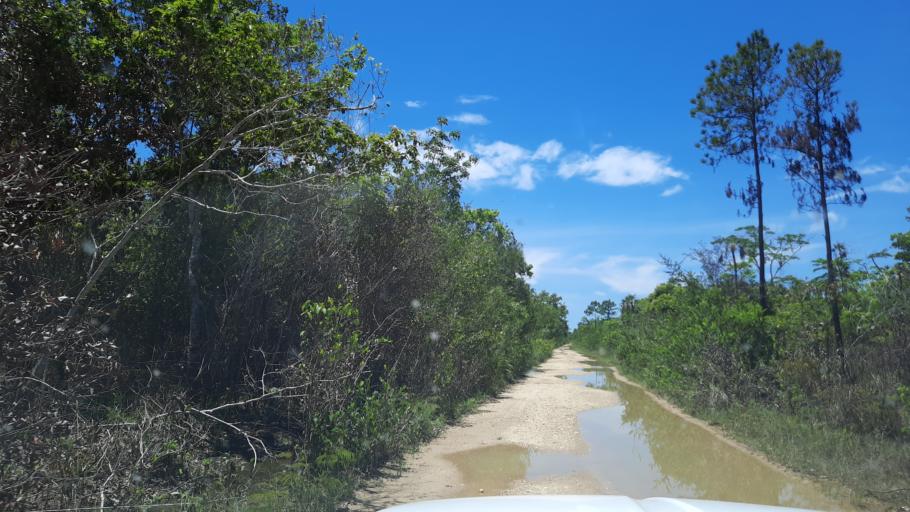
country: BZ
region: Cayo
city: Belmopan
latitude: 17.3762
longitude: -88.4877
